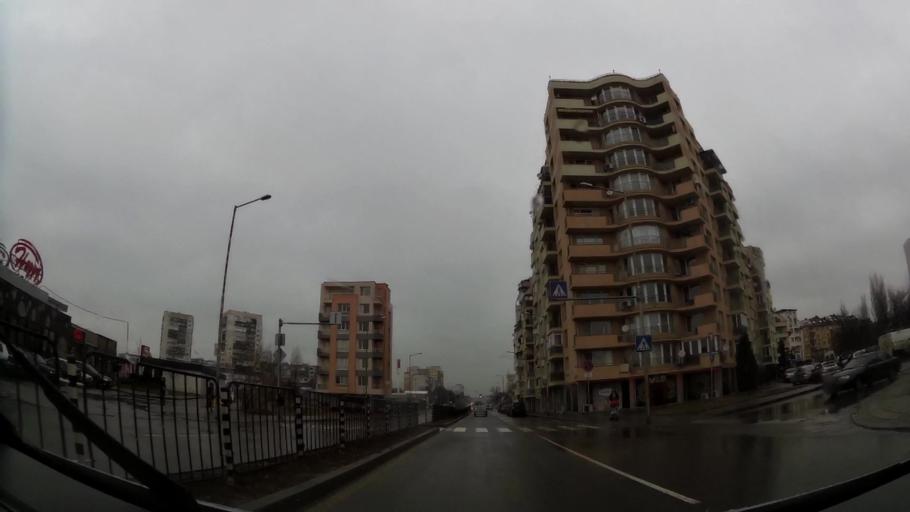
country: BG
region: Sofia-Capital
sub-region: Stolichna Obshtina
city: Sofia
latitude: 42.6484
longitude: 23.3798
